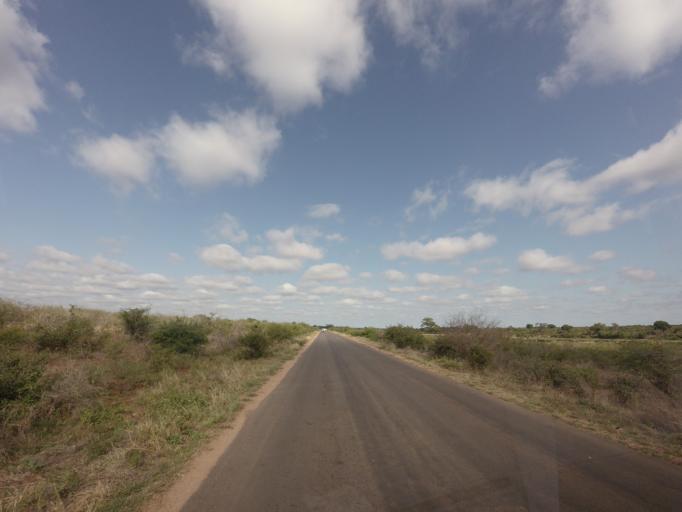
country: ZA
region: Mpumalanga
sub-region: Ehlanzeni District
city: Komatipoort
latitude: -25.1255
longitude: 31.9351
